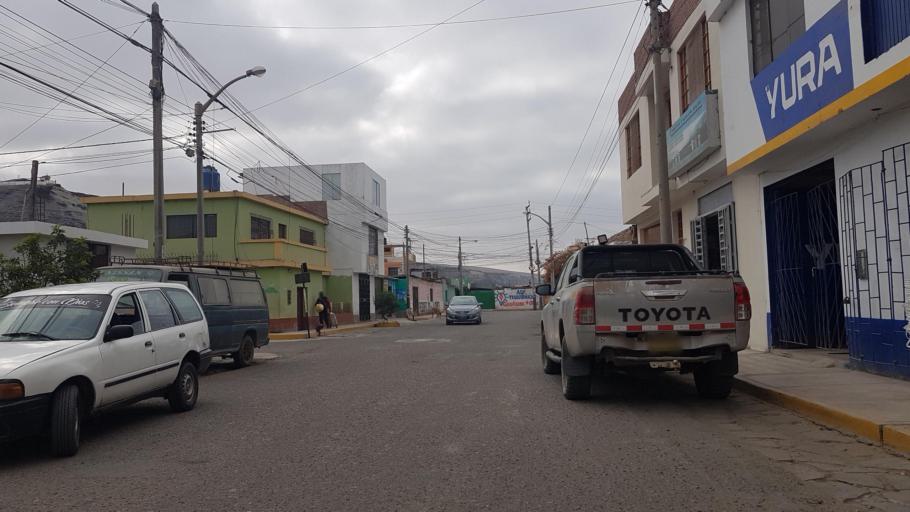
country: PE
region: Arequipa
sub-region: Provincia de Islay
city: Punta de Bombon
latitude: -17.1703
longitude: -71.7916
